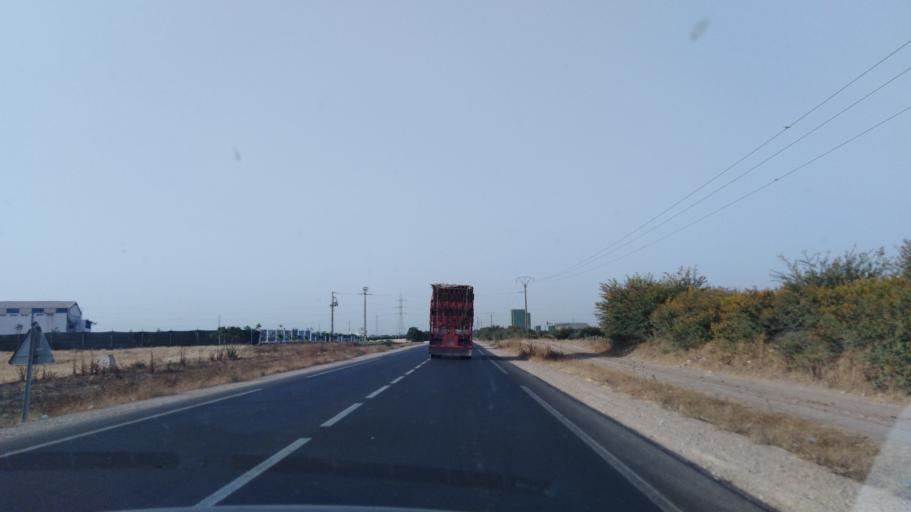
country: MA
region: Chaouia-Ouardigha
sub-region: Settat Province
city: Berrechid
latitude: 33.1401
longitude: -7.6242
